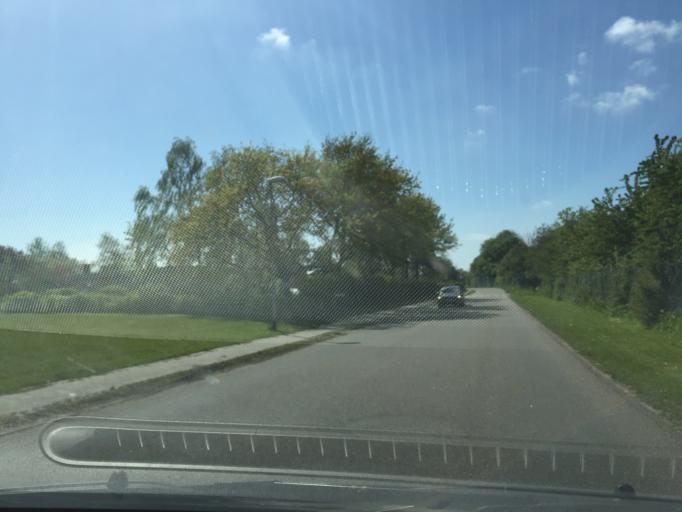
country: DK
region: Zealand
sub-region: Lolland Kommune
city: Rodby
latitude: 54.6885
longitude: 11.3901
